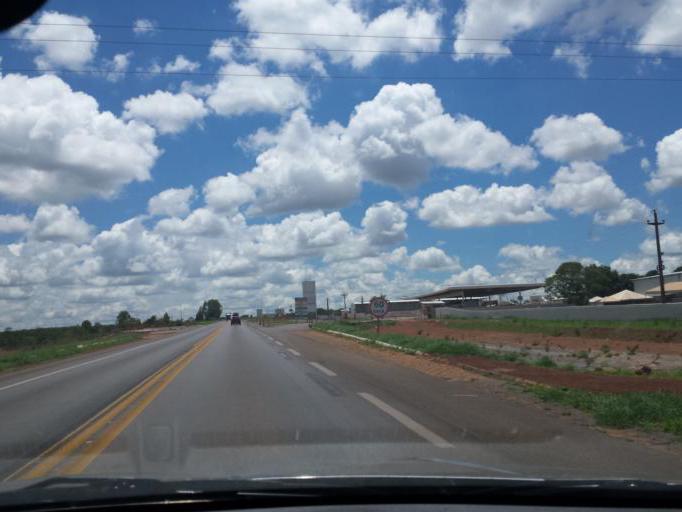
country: BR
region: Goias
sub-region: Cristalina
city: Cristalina
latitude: -16.7186
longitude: -47.6567
